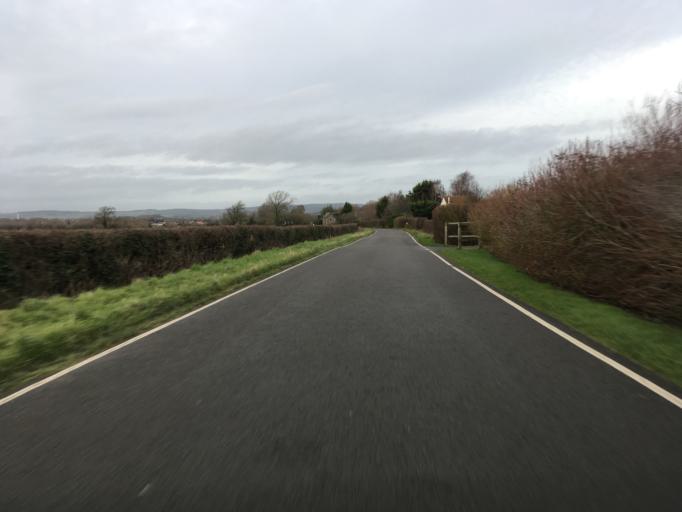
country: GB
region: Wales
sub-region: Monmouthshire
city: Magor
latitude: 51.5703
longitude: -2.8214
